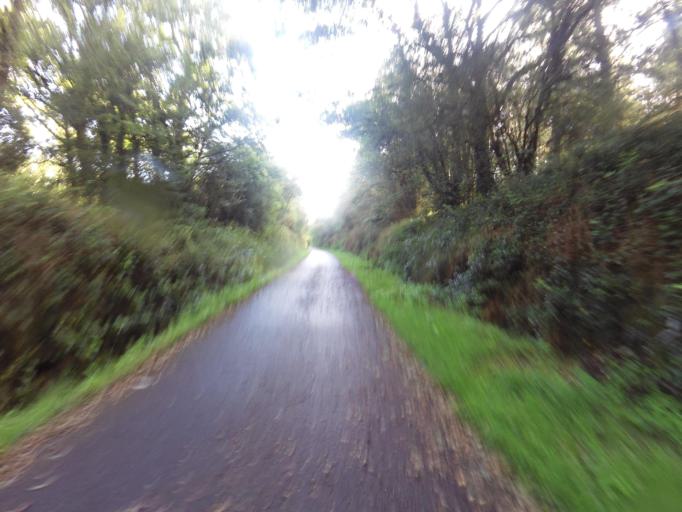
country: FR
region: Brittany
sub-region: Departement du Morbihan
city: Guillac
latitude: 47.9066
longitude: -2.4319
